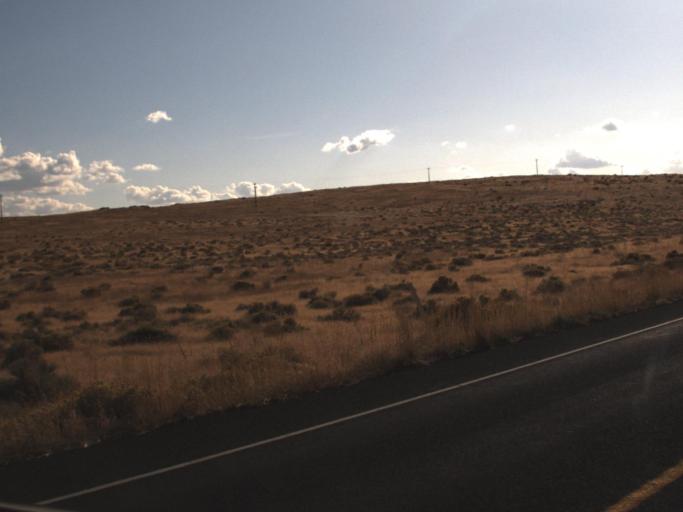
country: US
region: Oregon
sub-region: Morrow County
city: Boardman
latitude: 45.8842
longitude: -119.7211
